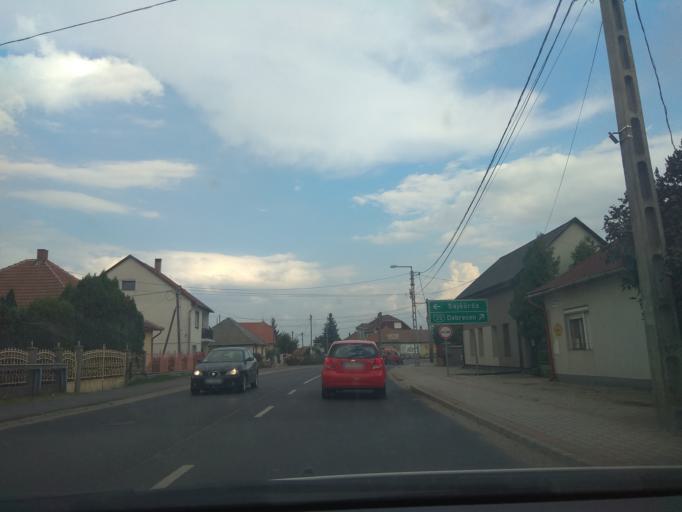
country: HU
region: Borsod-Abauj-Zemplen
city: Sajoszoged
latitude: 47.9462
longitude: 20.9947
